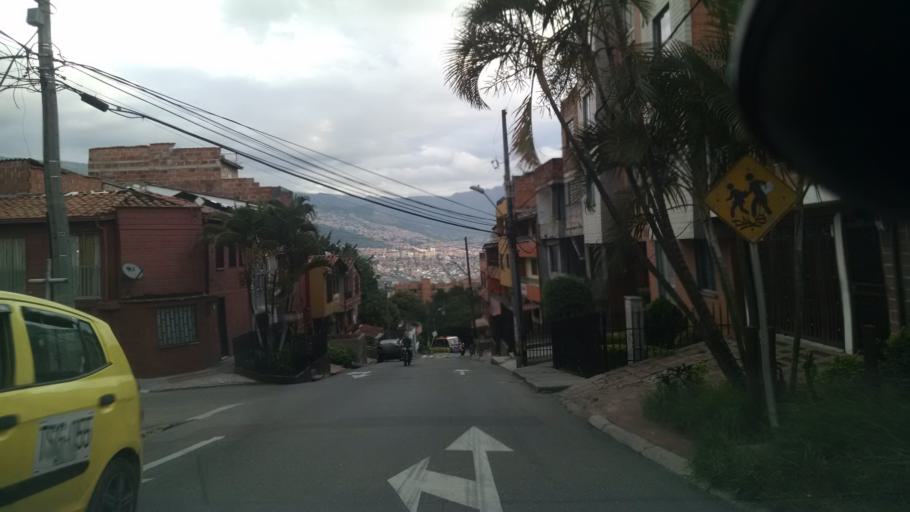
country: CO
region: Antioquia
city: Medellin
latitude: 6.2815
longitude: -75.5897
